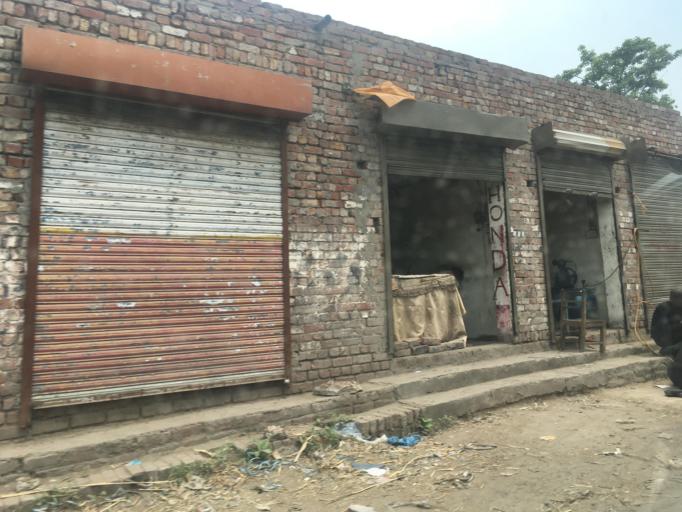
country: PK
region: Punjab
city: Lahore
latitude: 31.6152
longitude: 74.3674
